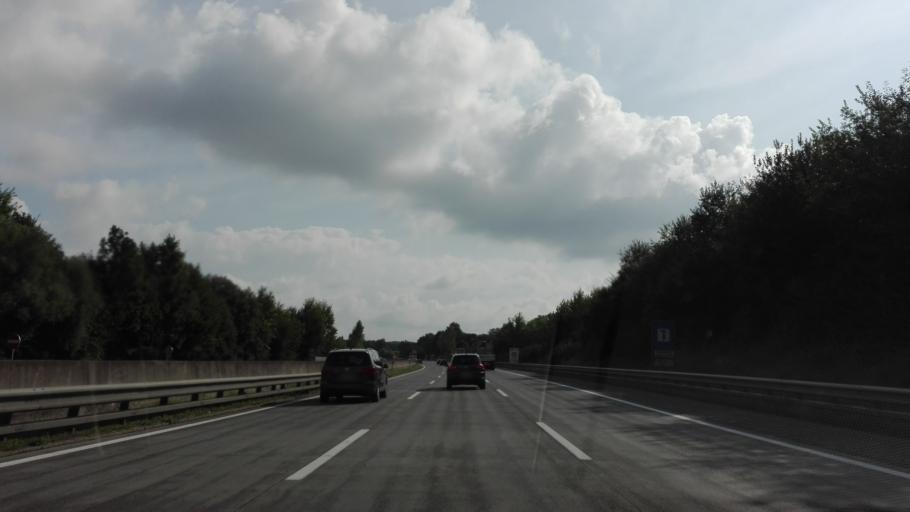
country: AT
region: Lower Austria
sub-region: Politischer Bezirk Amstetten
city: Zeillern
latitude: 48.1250
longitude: 14.8196
